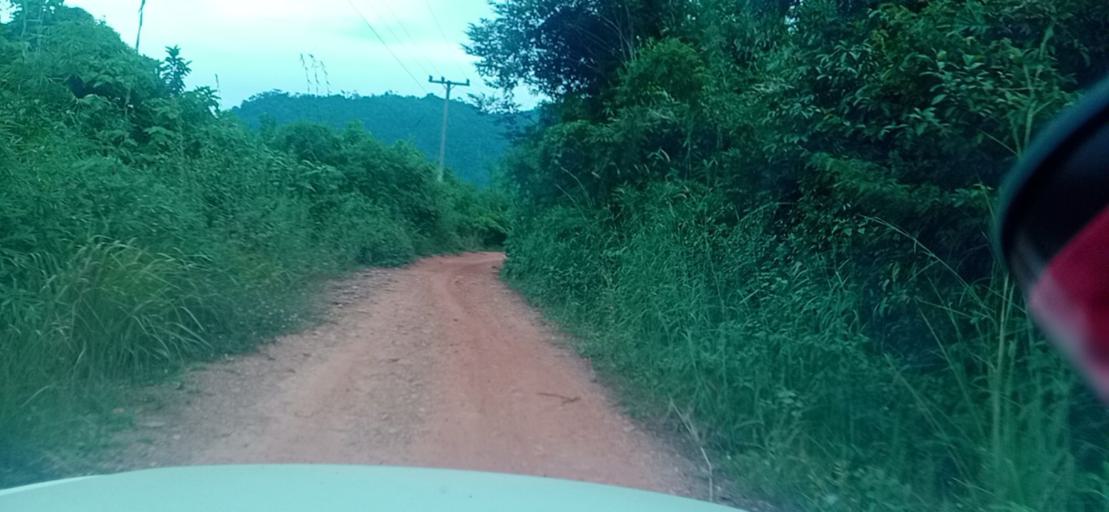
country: TH
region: Changwat Bueng Kan
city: Pak Khat
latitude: 18.5624
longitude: 103.2986
